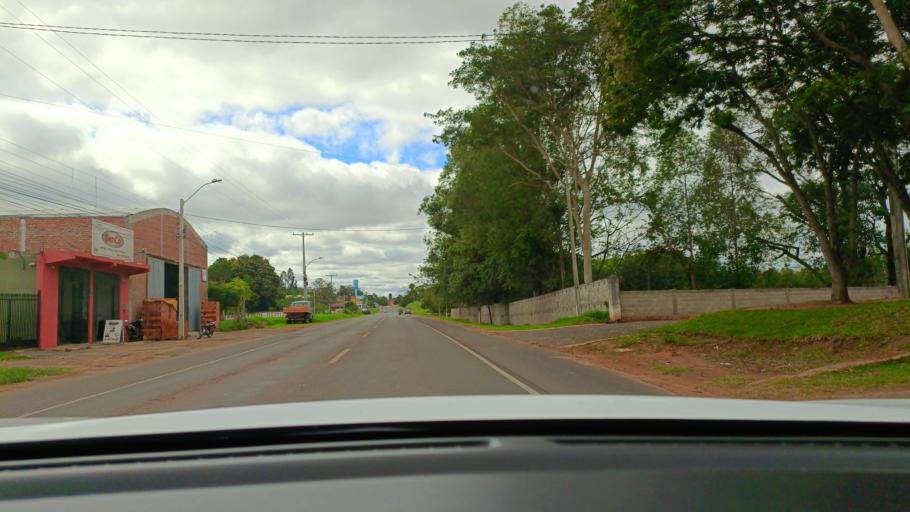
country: PY
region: San Pedro
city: Guayaybi
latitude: -24.6776
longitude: -56.4612
